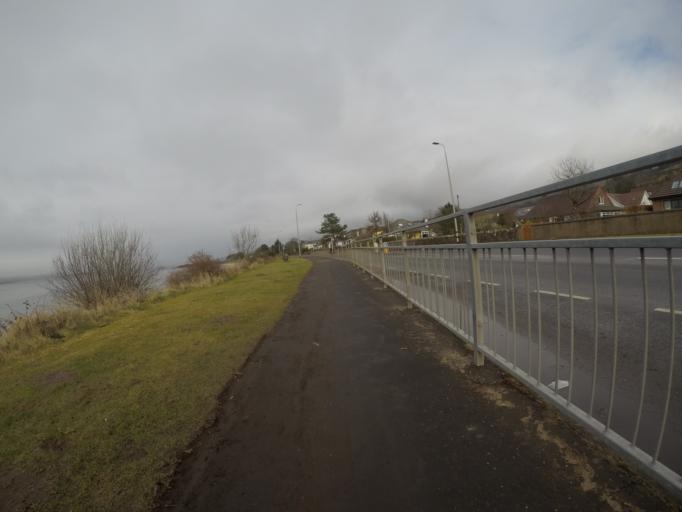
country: GB
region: Scotland
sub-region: North Ayrshire
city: Fairlie
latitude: 55.7481
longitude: -4.8570
